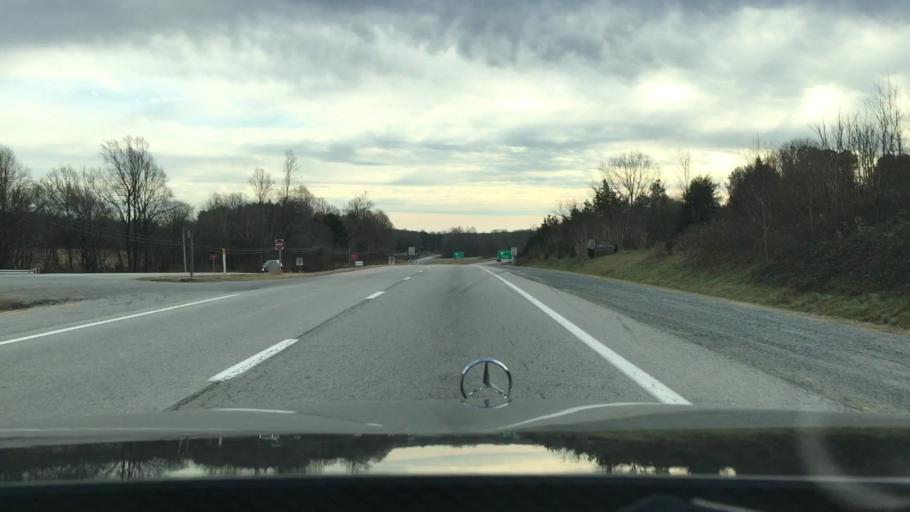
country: US
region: Virginia
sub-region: Pittsylvania County
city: Gretna
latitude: 36.9845
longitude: -79.3548
